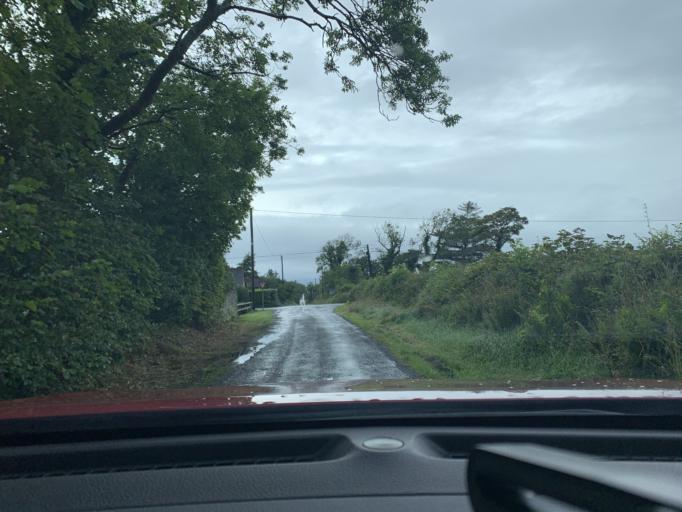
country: IE
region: Connaught
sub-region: Sligo
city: Strandhill
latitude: 54.3668
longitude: -8.5566
